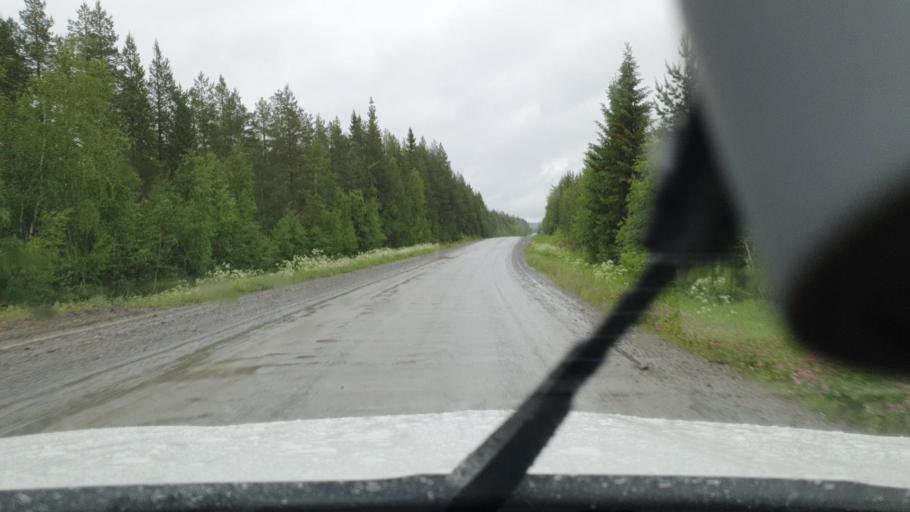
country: SE
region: Vaesterbotten
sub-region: Skelleftea Kommun
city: Burtraesk
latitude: 64.3794
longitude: 20.3435
